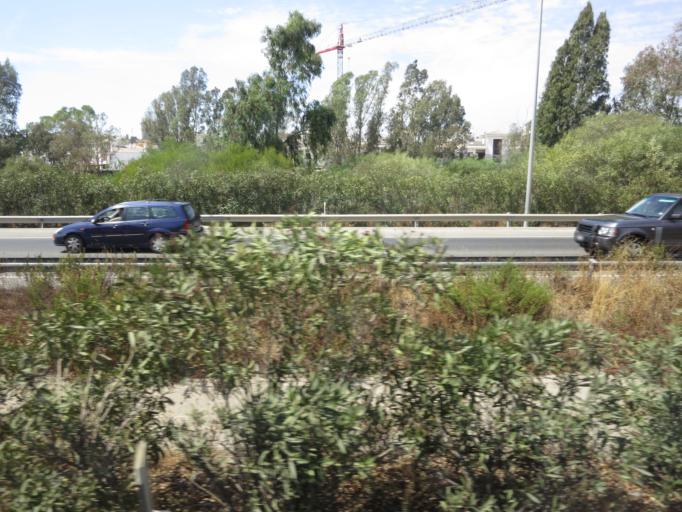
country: ES
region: Andalusia
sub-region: Provincia de Malaga
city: Marbella
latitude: 36.5068
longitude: -4.9480
